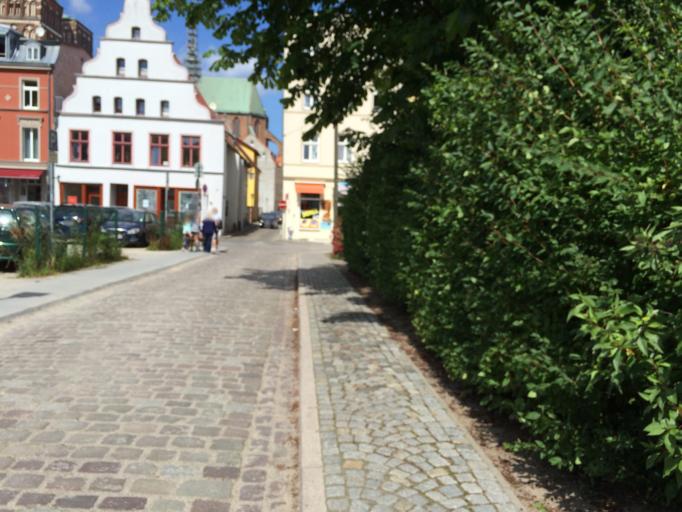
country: DE
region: Mecklenburg-Vorpommern
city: Stralsund
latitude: 54.3137
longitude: 13.0923
